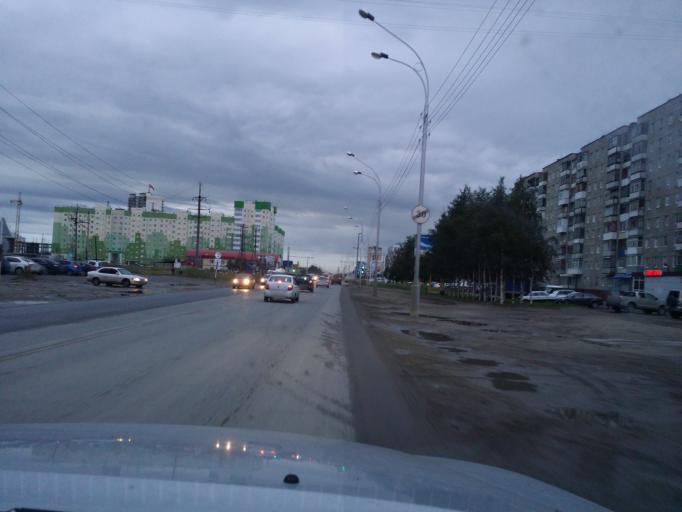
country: RU
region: Khanty-Mansiyskiy Avtonomnyy Okrug
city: Nizhnevartovsk
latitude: 60.9361
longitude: 76.6143
